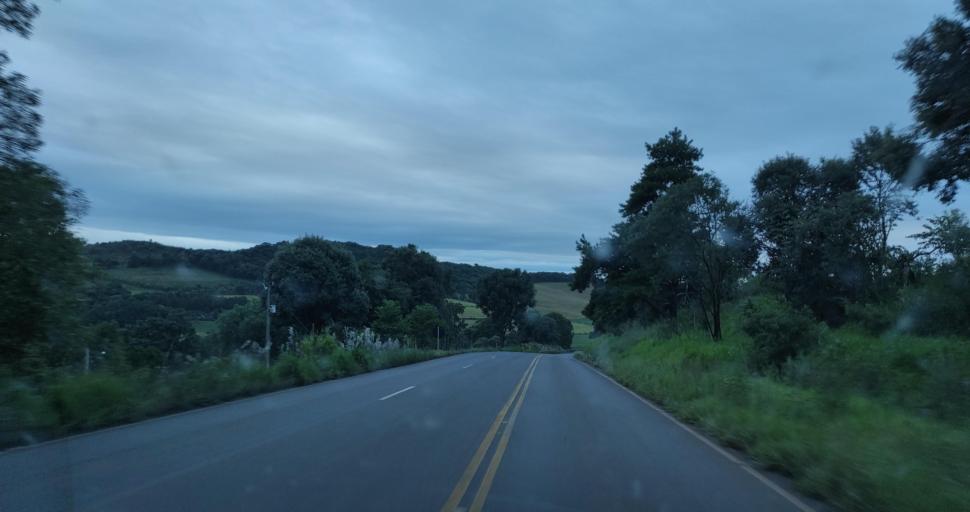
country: BR
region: Santa Catarina
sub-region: Xanxere
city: Xanxere
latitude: -26.7150
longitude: -52.4146
